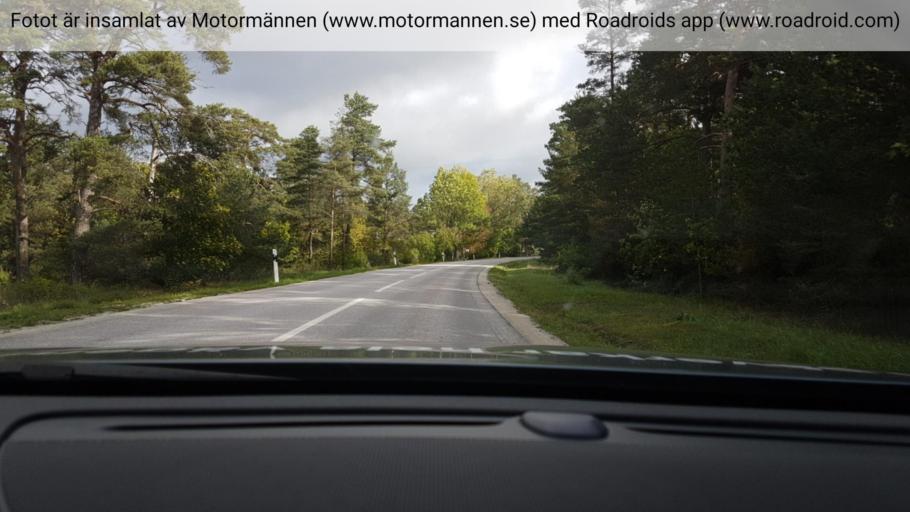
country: SE
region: Gotland
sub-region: Gotland
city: Visby
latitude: 57.6744
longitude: 18.4850
